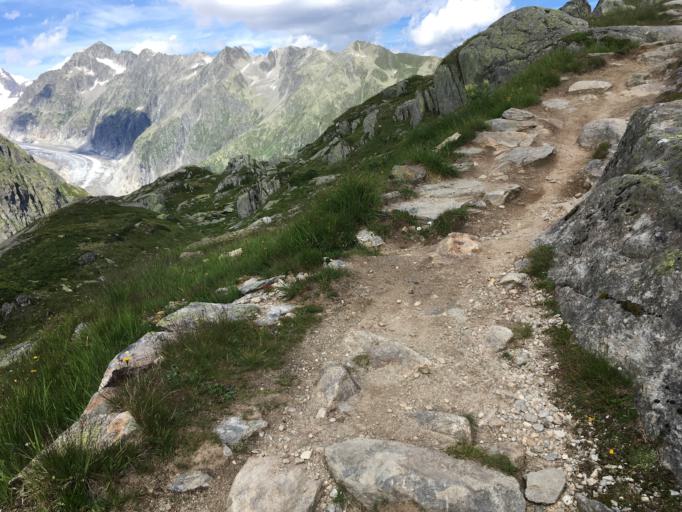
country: CH
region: Valais
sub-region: Goms District
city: Fiesch
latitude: 46.4448
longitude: 8.1150
